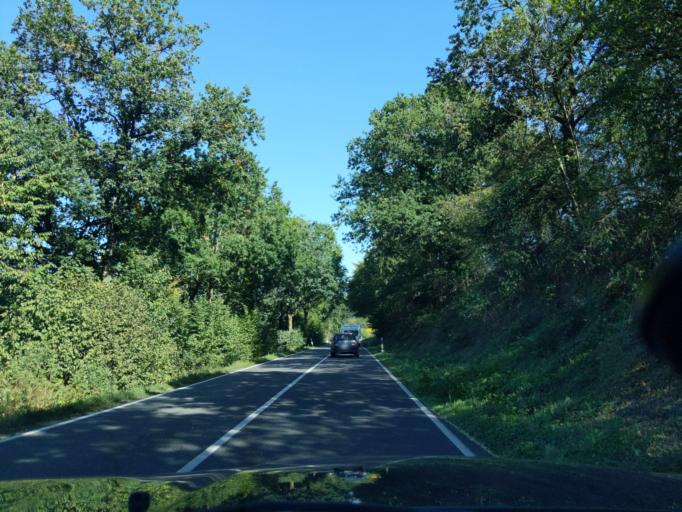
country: DE
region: North Rhine-Westphalia
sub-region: Regierungsbezirk Koln
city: Eitorf
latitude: 50.7738
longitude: 7.3700
